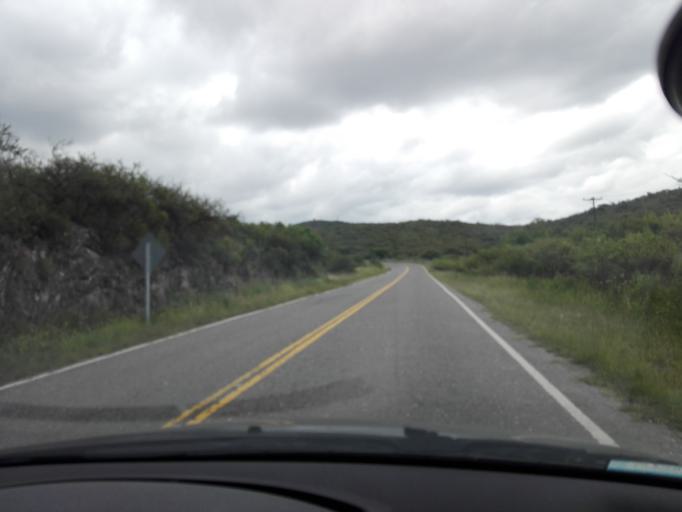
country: AR
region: Cordoba
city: Alta Gracia
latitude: -31.5919
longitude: -64.4985
